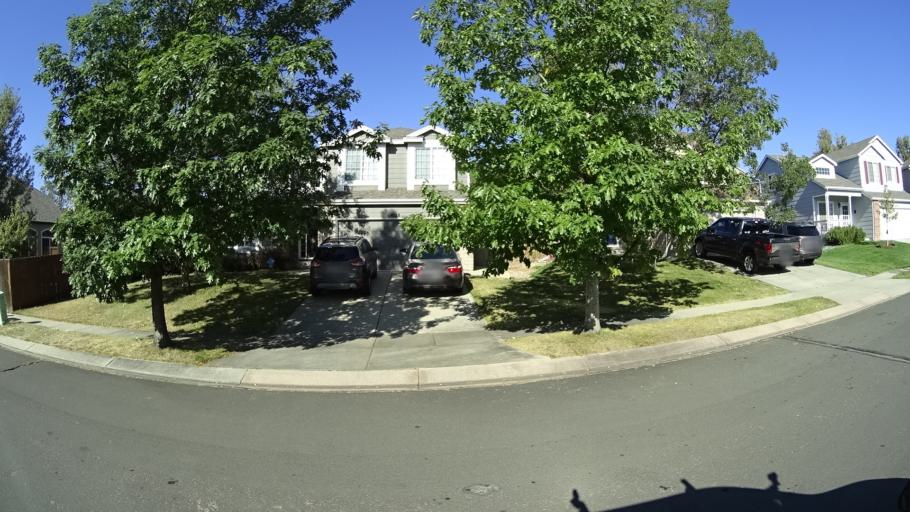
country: US
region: Colorado
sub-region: El Paso County
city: Cimarron Hills
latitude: 38.8904
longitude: -104.6975
